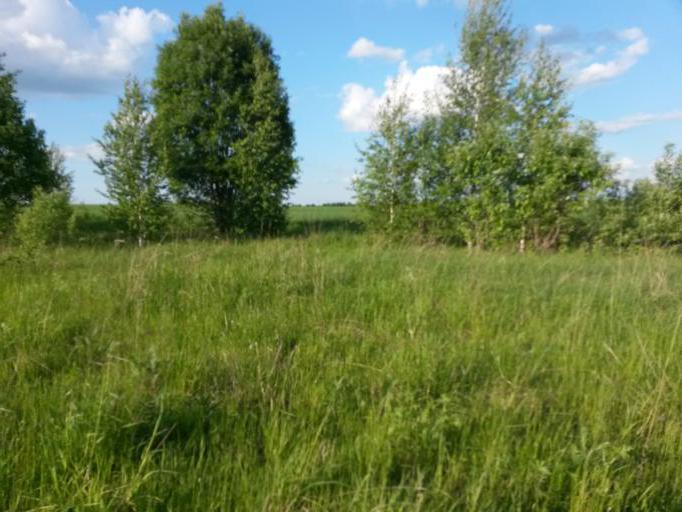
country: RU
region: Jaroslavl
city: Burmakino
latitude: 57.3577
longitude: 40.2017
